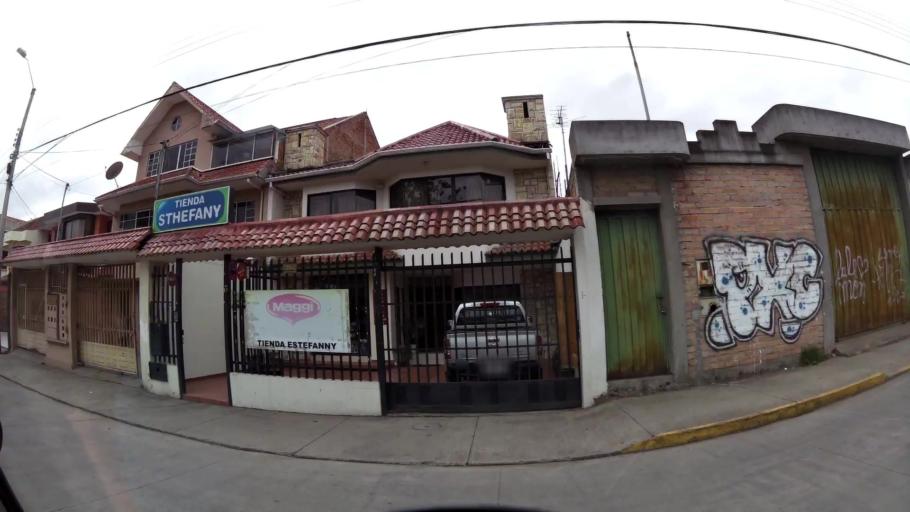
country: EC
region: Azuay
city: Cuenca
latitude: -2.9095
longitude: -79.0321
